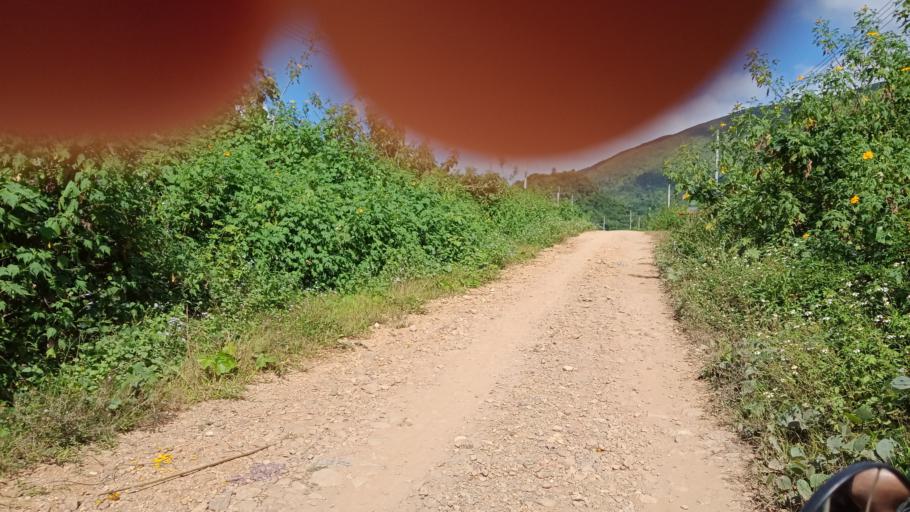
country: LA
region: Xiangkhoang
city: Phonsavan
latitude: 19.1088
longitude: 102.9275
